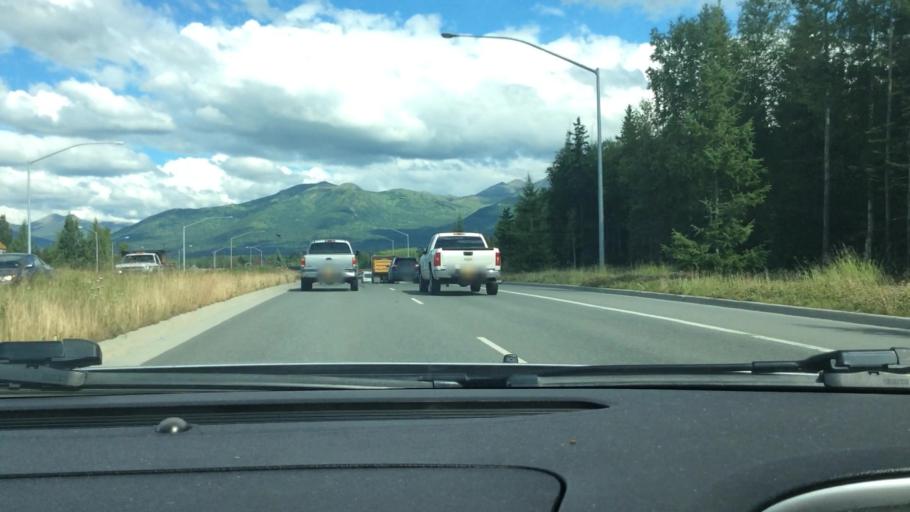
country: US
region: Alaska
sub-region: Anchorage Municipality
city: Anchorage
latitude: 61.1782
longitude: -149.7850
